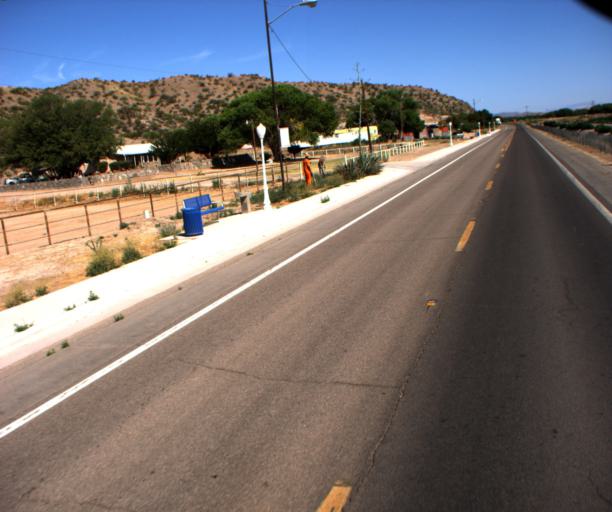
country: US
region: Arizona
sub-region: Greenlee County
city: Clifton
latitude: 32.7273
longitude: -109.1096
